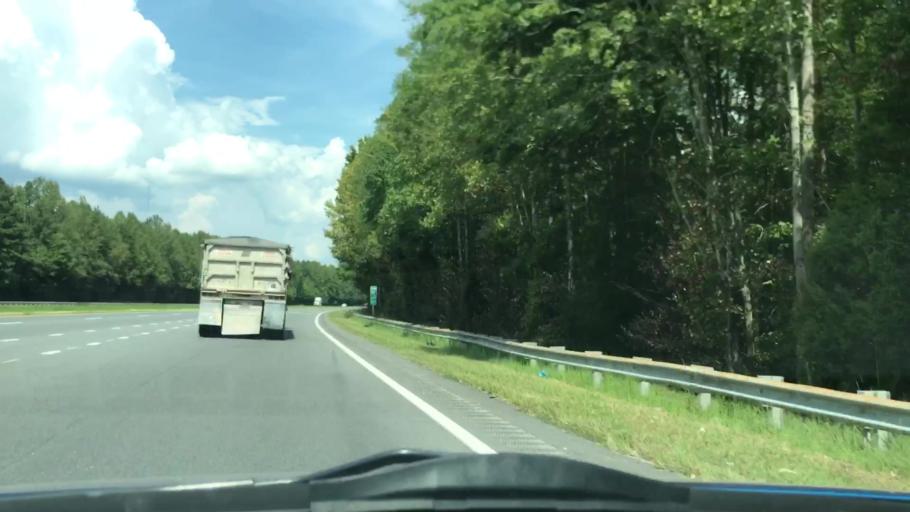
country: US
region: North Carolina
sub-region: Randolph County
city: Randleman
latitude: 35.8296
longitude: -79.8268
